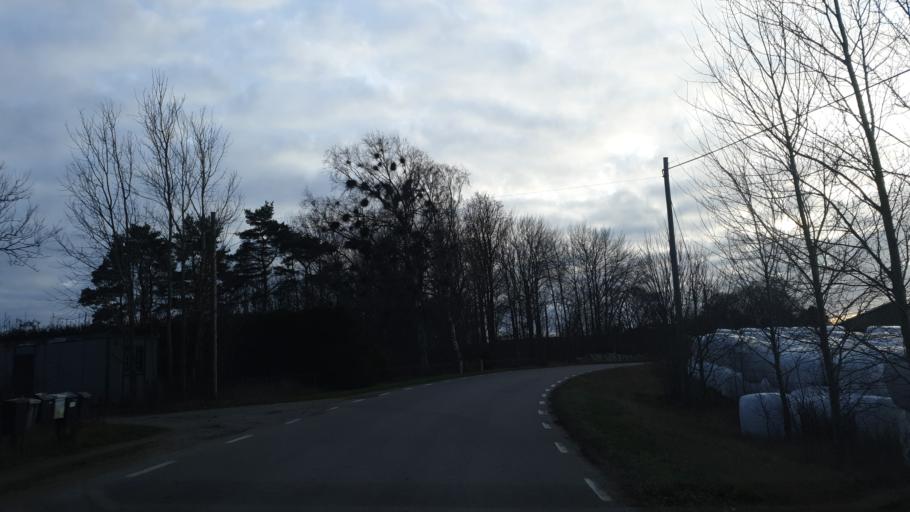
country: SE
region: Blekinge
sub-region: Karlskrona Kommun
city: Jaemjoe
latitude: 56.1910
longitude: 15.9477
